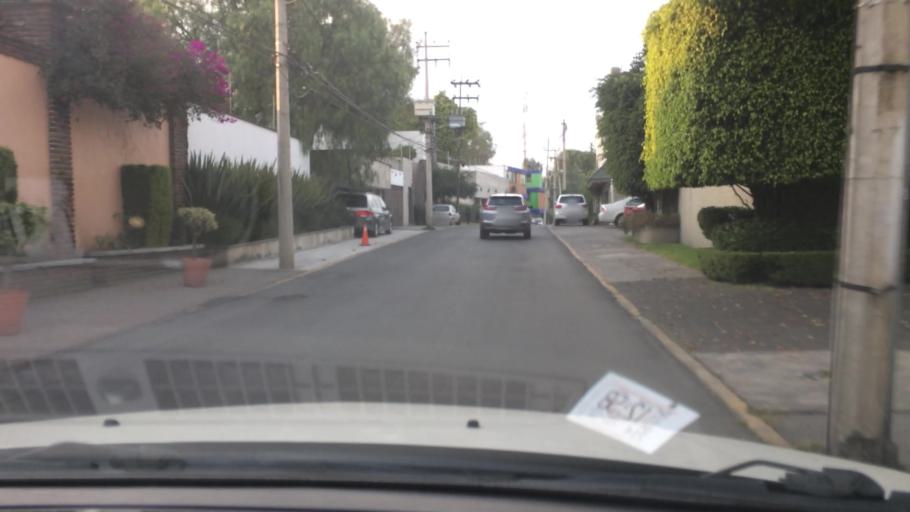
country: MX
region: Mexico City
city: Magdalena Contreras
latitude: 19.3229
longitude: -99.2121
